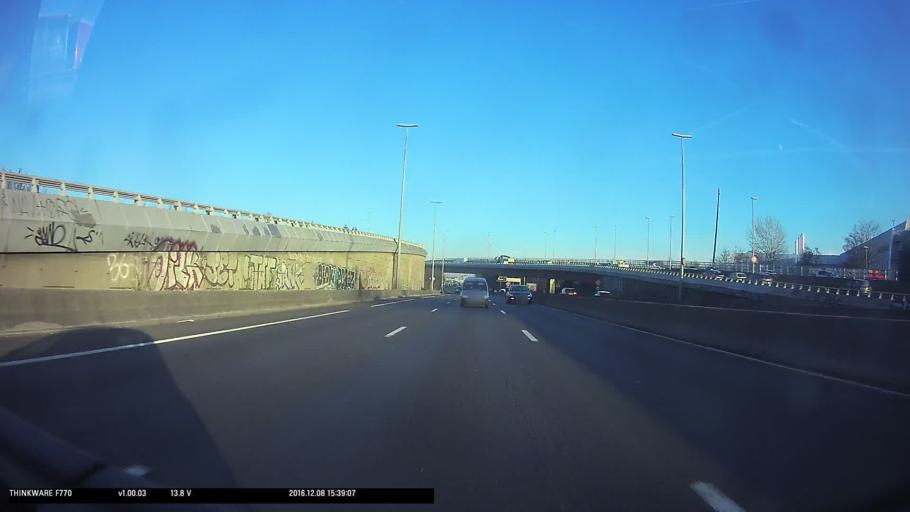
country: FR
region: Ile-de-France
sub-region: Departement de Seine-Saint-Denis
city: La Courneuve
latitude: 48.9261
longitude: 2.4005
